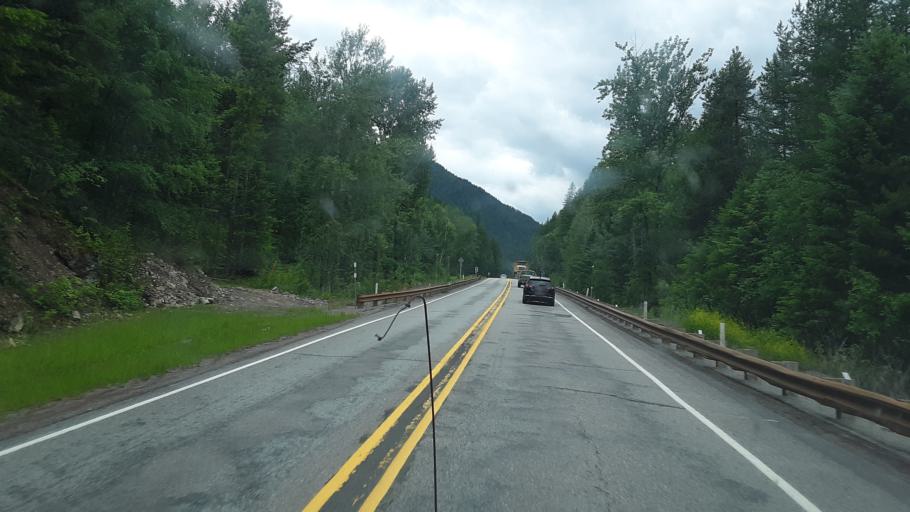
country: US
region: Montana
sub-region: Flathead County
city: Columbia Falls
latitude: 48.4944
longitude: -113.8864
